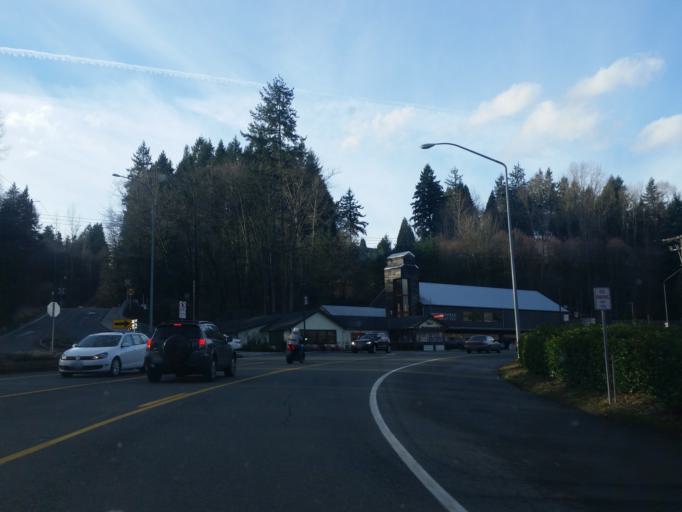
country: US
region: Washington
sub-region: King County
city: Woodinville
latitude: 47.7330
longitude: -122.1518
